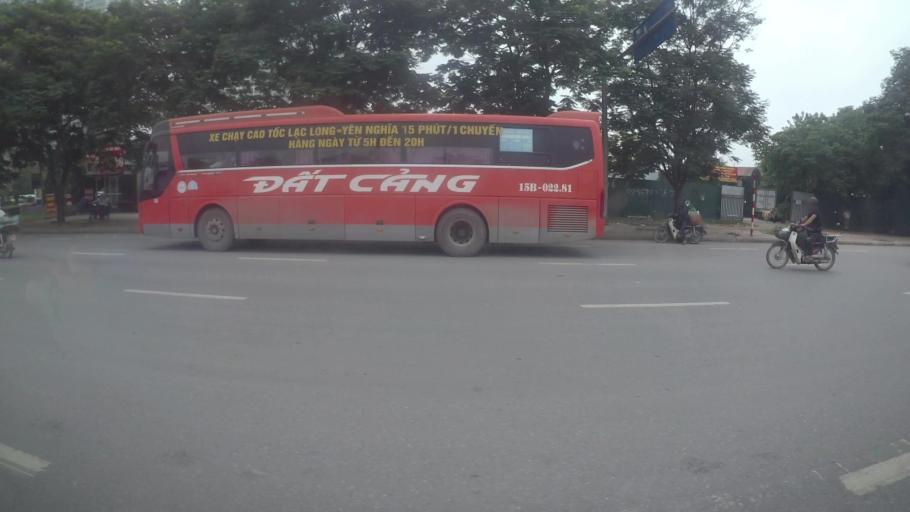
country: VN
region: Ha Noi
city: Thanh Xuan
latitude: 21.0032
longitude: 105.7903
